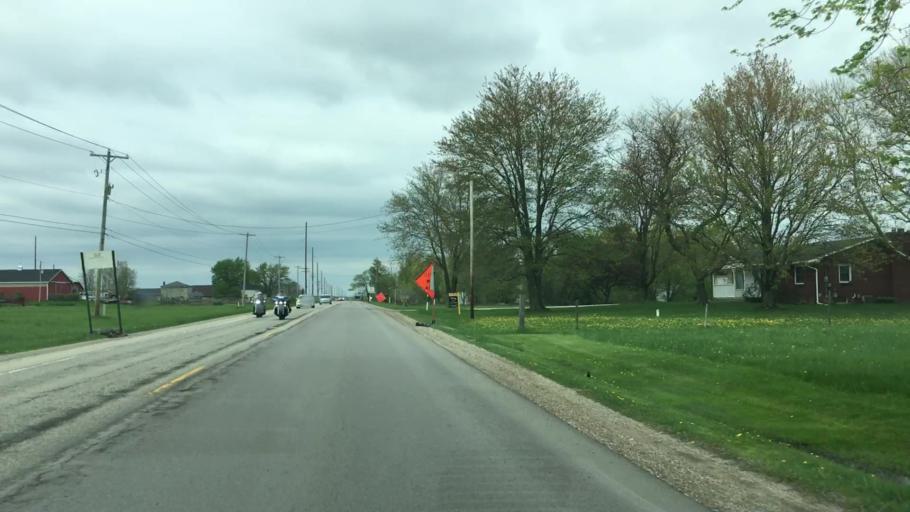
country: US
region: Michigan
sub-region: Ottawa County
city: Hudsonville
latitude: 42.8299
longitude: -85.8619
